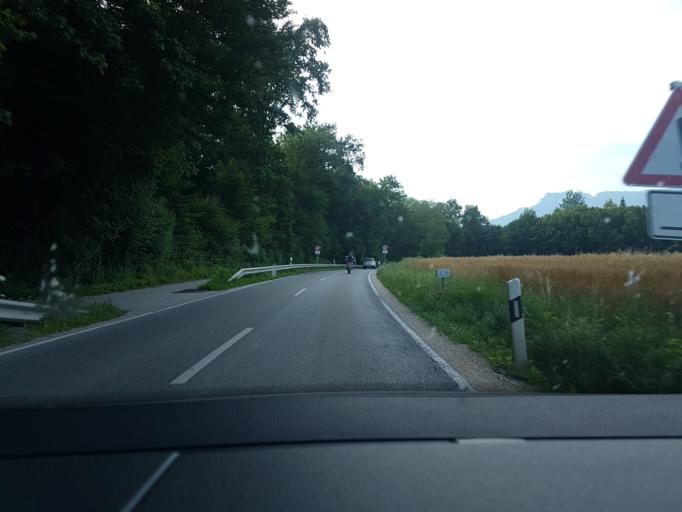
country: DE
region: Bavaria
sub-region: Upper Bavaria
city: Ainring
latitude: 47.8496
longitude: 12.9432
